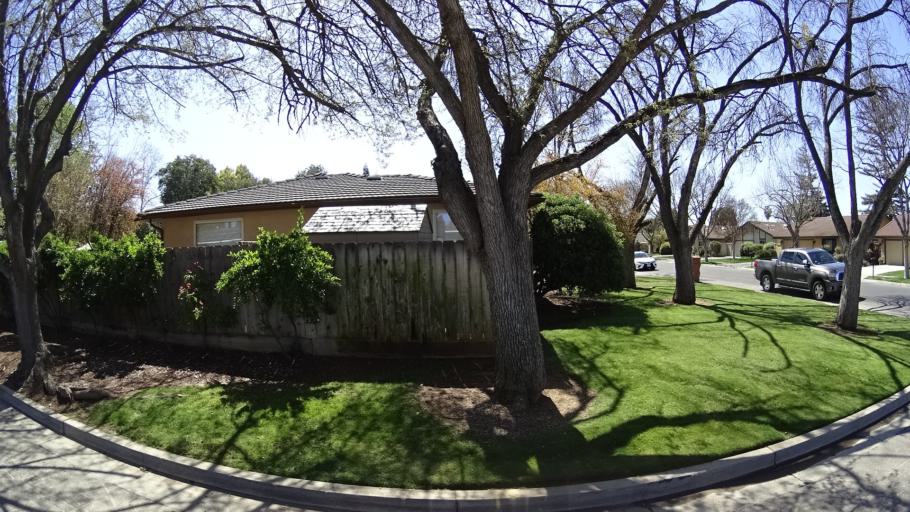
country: US
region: California
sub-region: Fresno County
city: Fresno
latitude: 36.8112
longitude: -119.7960
